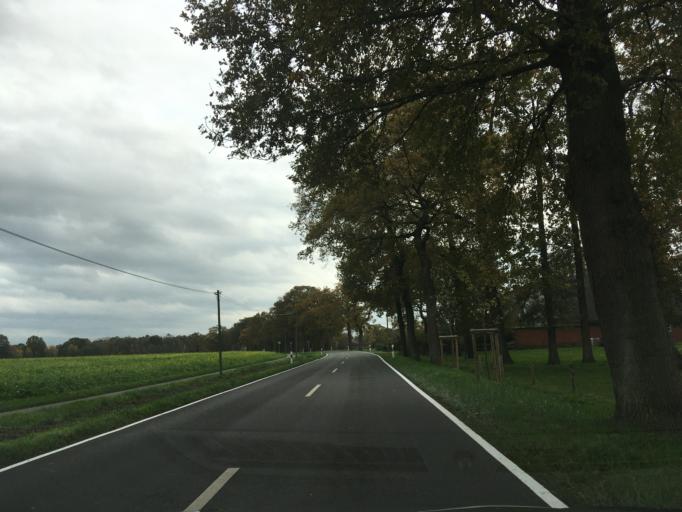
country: DE
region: North Rhine-Westphalia
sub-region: Regierungsbezirk Munster
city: Vreden
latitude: 52.0875
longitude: 6.8922
